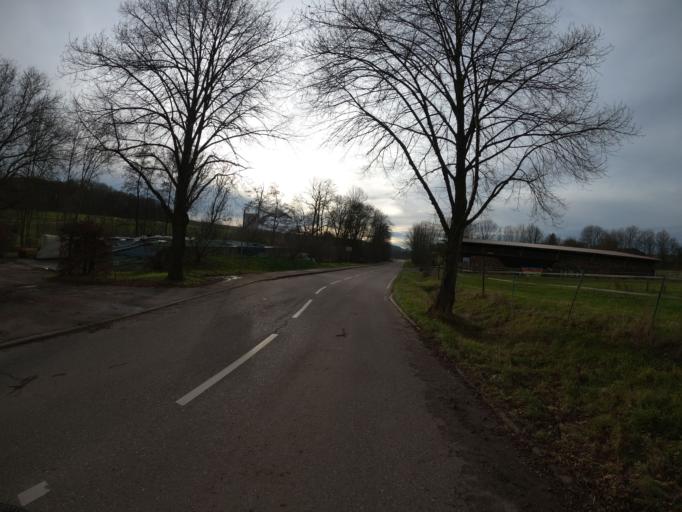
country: DE
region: Baden-Wuerttemberg
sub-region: Regierungsbezirk Stuttgart
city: Birenbach
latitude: 48.7306
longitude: 9.6820
